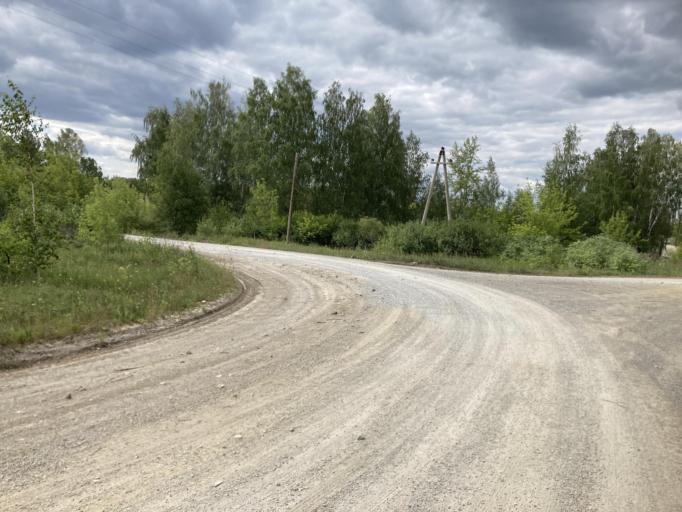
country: RU
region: Sverdlovsk
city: Bogdanovich
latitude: 56.7924
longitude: 62.0616
